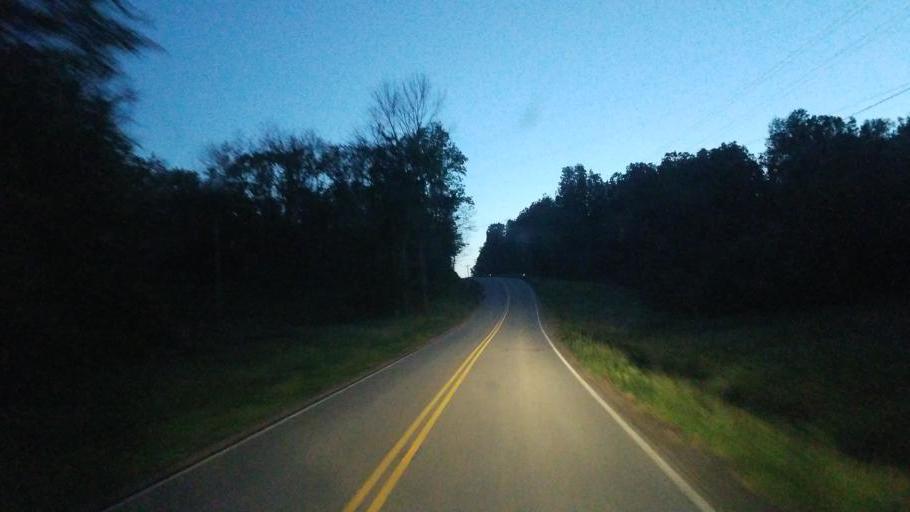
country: US
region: Ohio
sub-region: Belmont County
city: Barnesville
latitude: 40.0651
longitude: -81.3256
